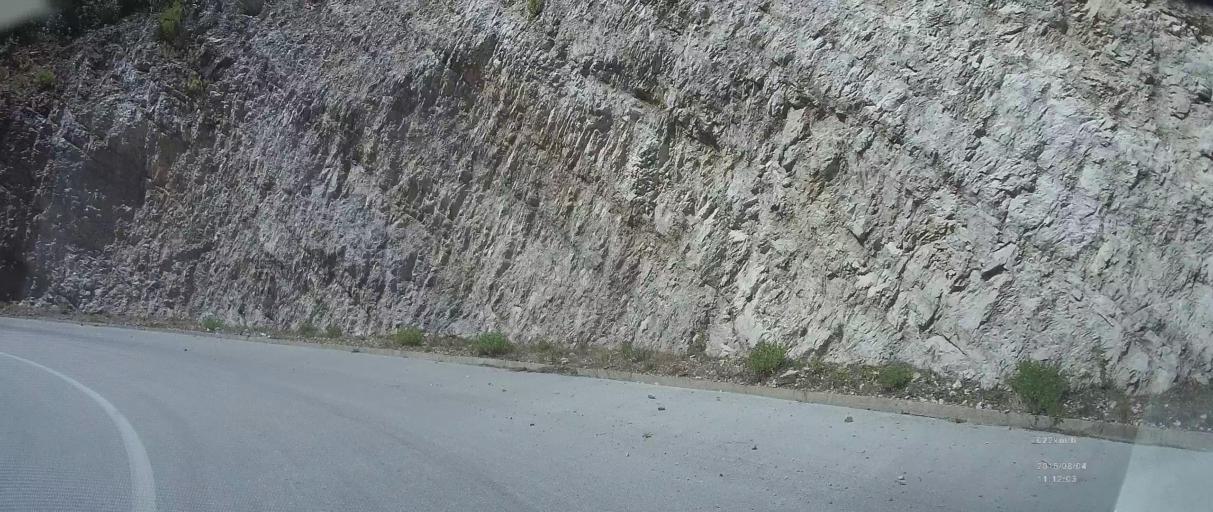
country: HR
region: Dubrovacko-Neretvanska
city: Blato
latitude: 42.7585
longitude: 17.4716
